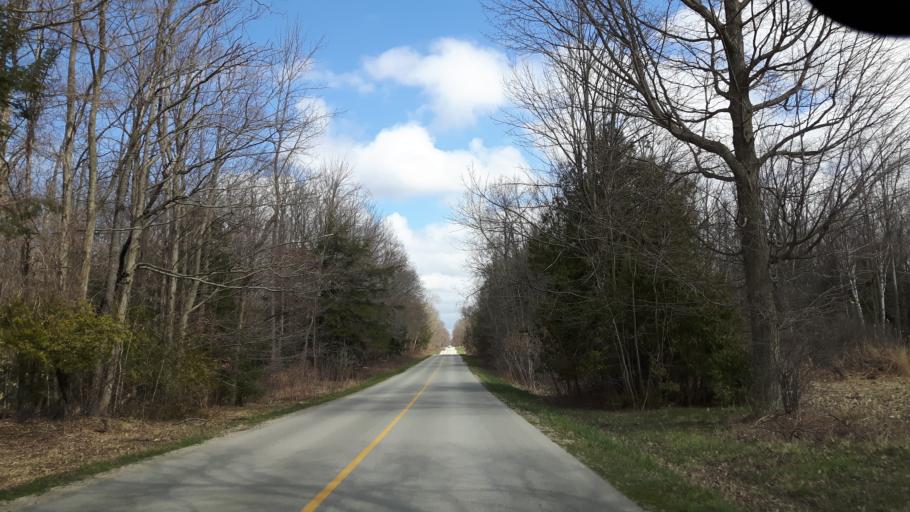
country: CA
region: Ontario
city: Goderich
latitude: 43.6175
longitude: -81.6846
